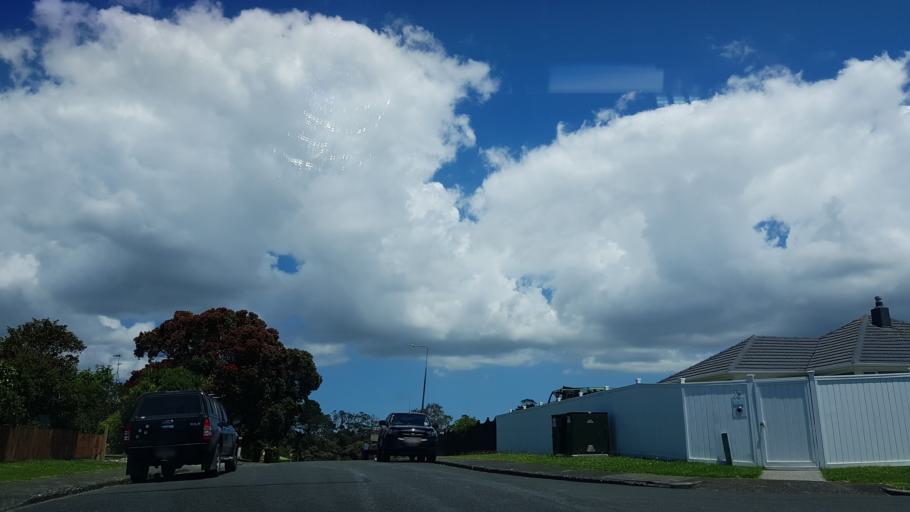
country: NZ
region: Auckland
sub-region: Auckland
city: North Shore
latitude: -36.7874
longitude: 174.6931
